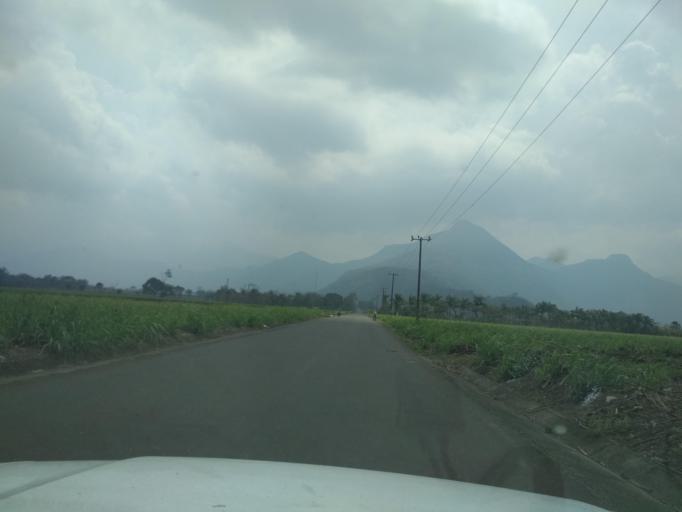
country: MX
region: Veracruz
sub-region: Cordoba
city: San Jose de Tapia
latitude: 18.8447
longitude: -96.9797
